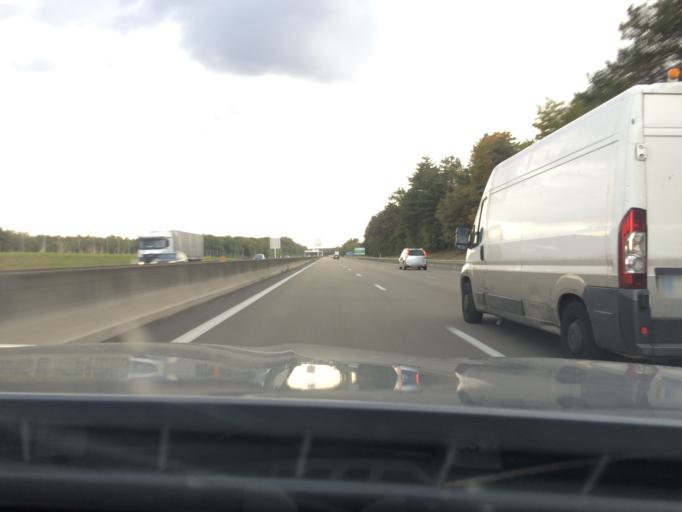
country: FR
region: Ile-de-France
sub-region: Departement de Seine-et-Marne
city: Bagneaux-sur-Loing
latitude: 48.2313
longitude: 2.7582
